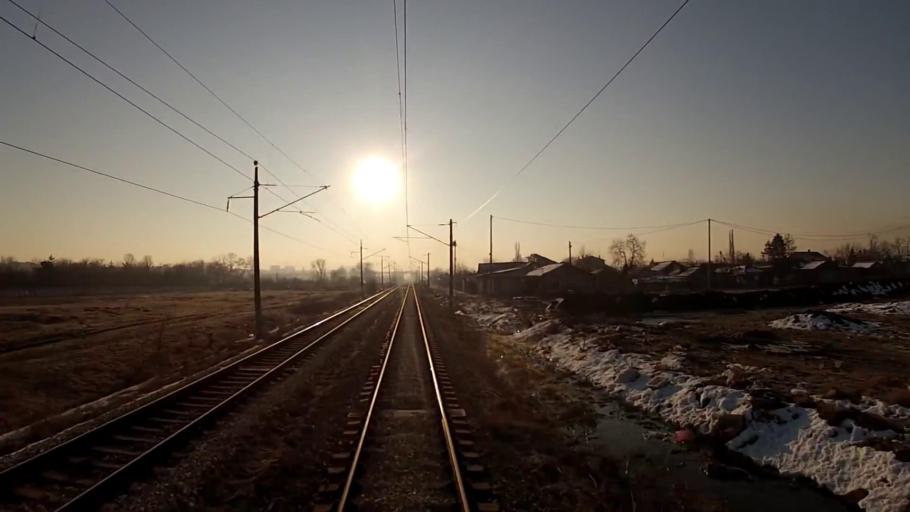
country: BG
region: Sofiya
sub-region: Obshtina Bozhurishte
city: Bozhurishte
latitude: 42.7389
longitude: 23.2634
